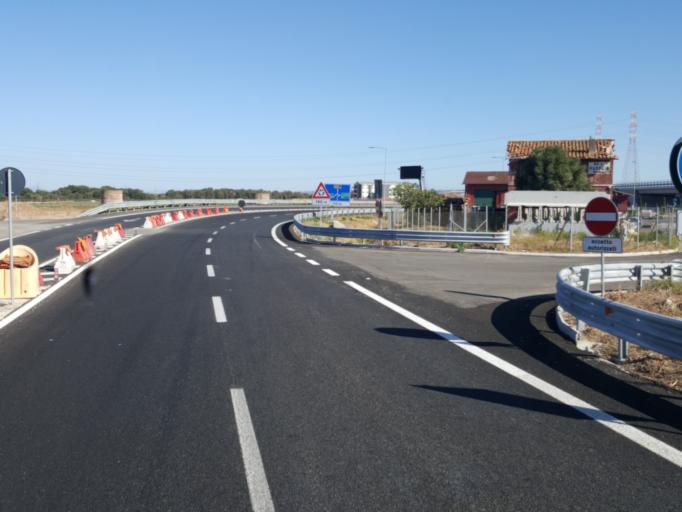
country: IT
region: Latium
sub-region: Citta metropolitana di Roma Capitale
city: Aurelia
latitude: 42.1621
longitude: 11.7883
